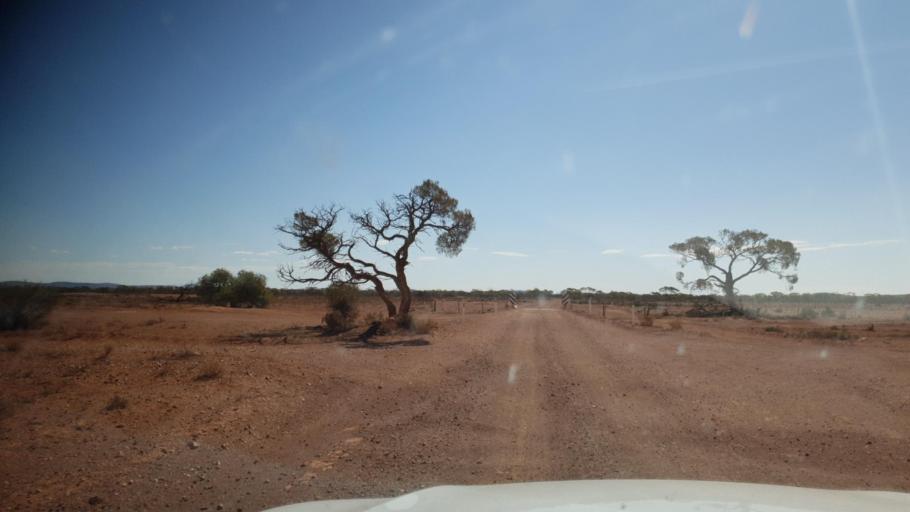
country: AU
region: South Australia
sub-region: Kimba
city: Caralue
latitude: -32.5010
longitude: 136.0932
